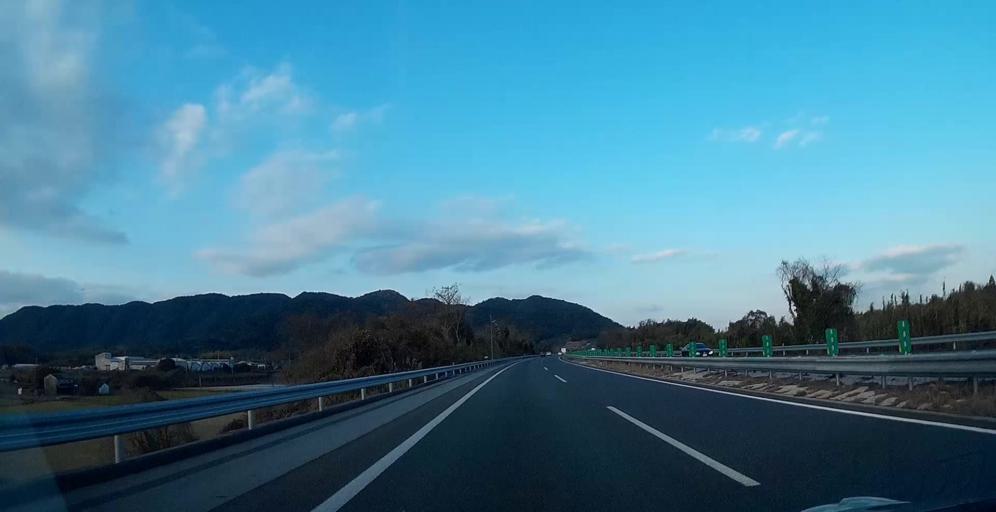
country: JP
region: Kumamoto
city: Uto
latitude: 32.6679
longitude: 130.7132
